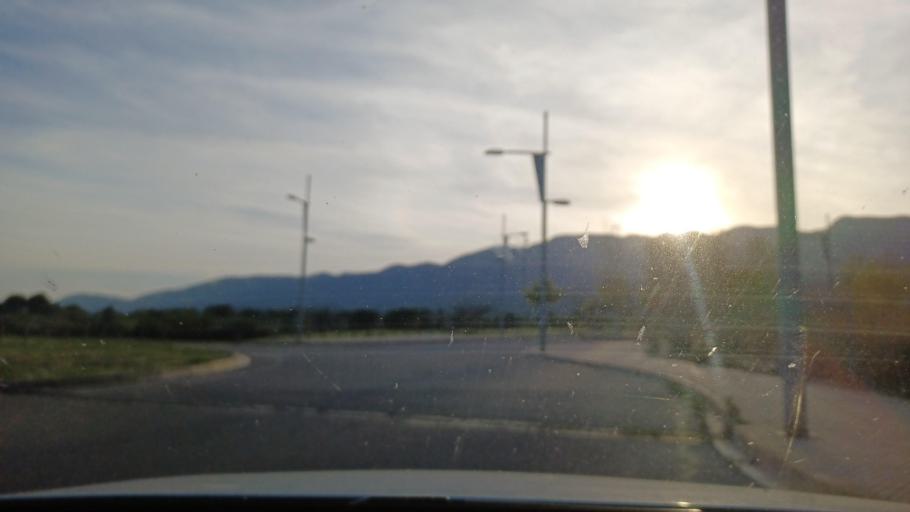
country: ES
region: Catalonia
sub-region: Provincia de Tarragona
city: Sant Carles de la Rapita
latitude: 40.6151
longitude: 0.5821
